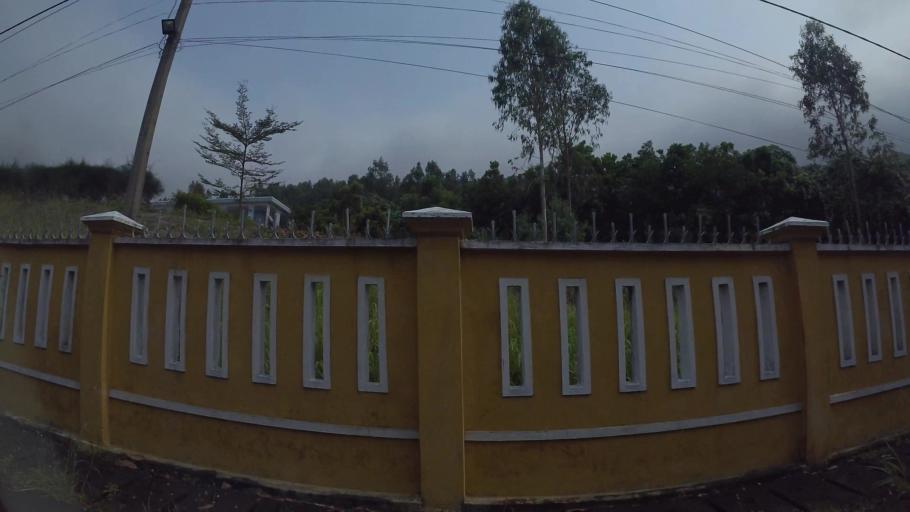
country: VN
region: Da Nang
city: Son Tra
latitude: 16.1094
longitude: 108.2599
